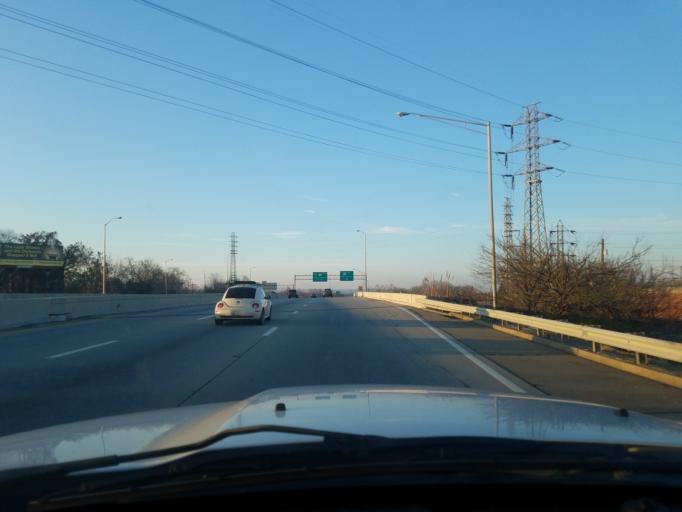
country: US
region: Kentucky
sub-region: Jefferson County
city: Louisville
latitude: 38.2689
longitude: -85.7816
